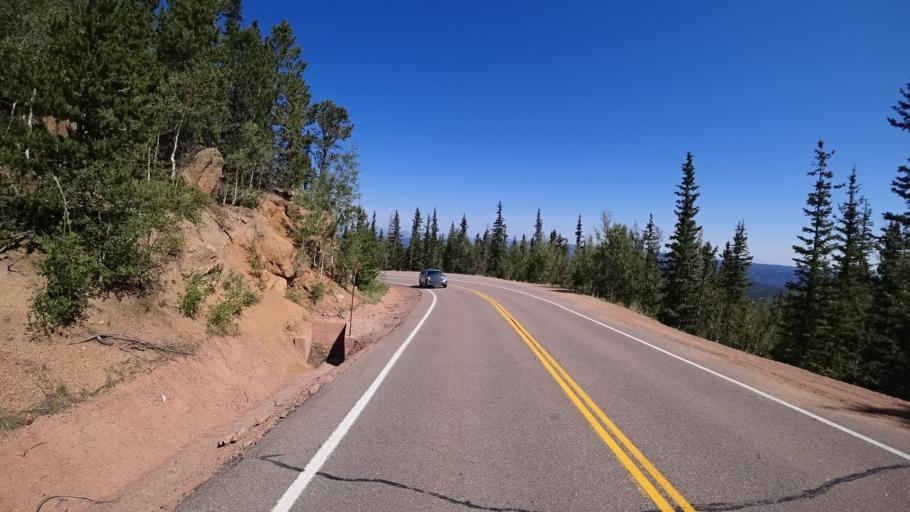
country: US
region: Colorado
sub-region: El Paso County
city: Cascade-Chipita Park
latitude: 38.8918
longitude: -105.0677
